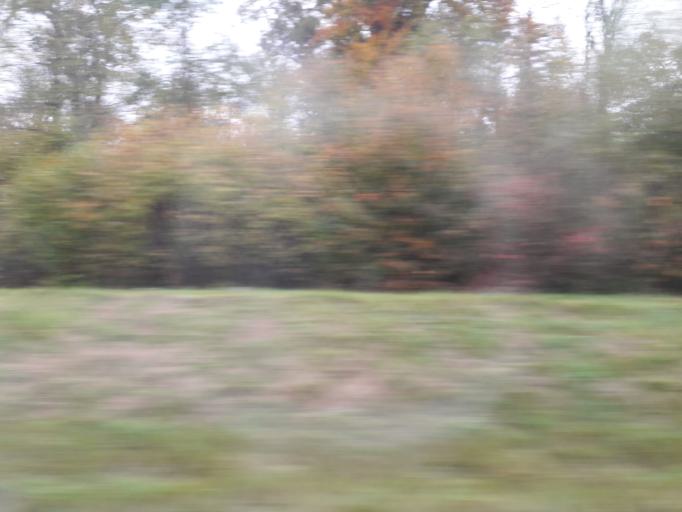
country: CH
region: Bern
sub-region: Emmental District
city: Oberburg
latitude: 47.0323
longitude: 7.6365
